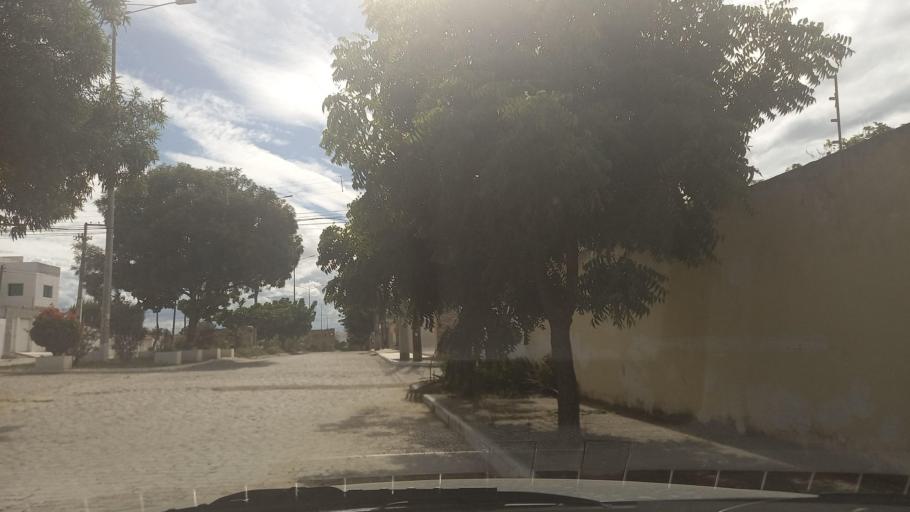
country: BR
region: Pernambuco
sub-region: Caruaru
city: Caruaru
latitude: -8.2917
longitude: -35.9897
